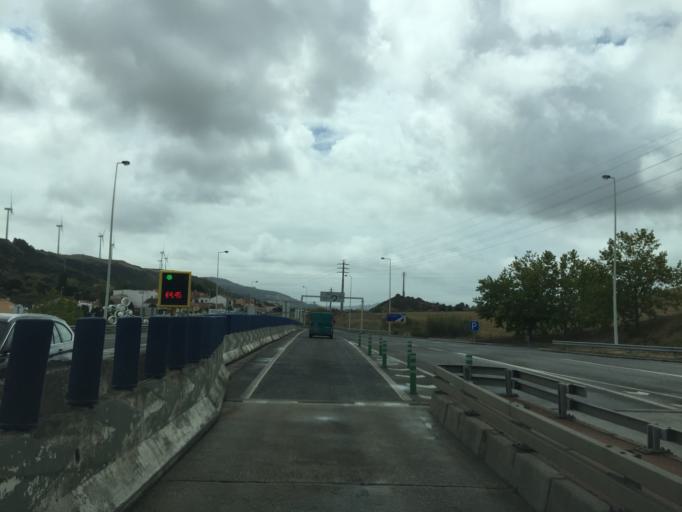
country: PT
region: Lisbon
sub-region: Torres Vedras
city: Torres Vedras
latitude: 39.0617
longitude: -9.2425
